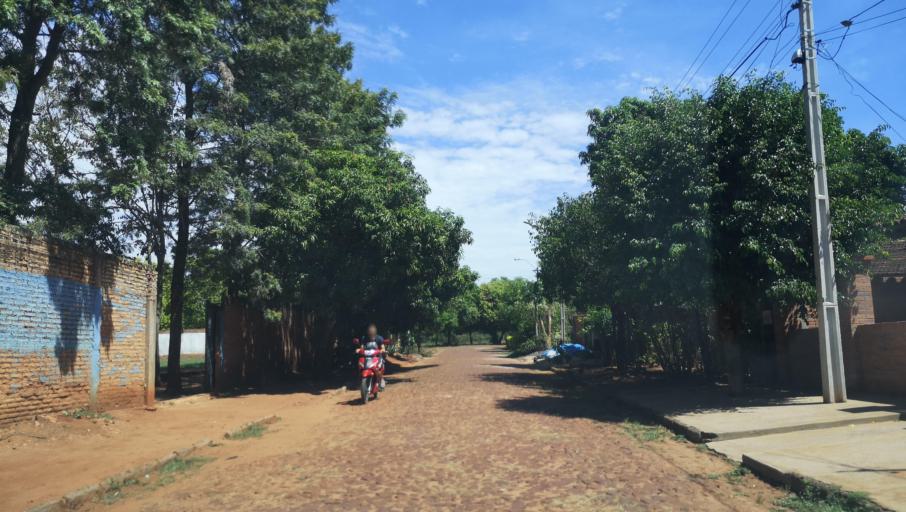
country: PY
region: Misiones
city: Santa Maria
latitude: -26.8955
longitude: -57.0296
